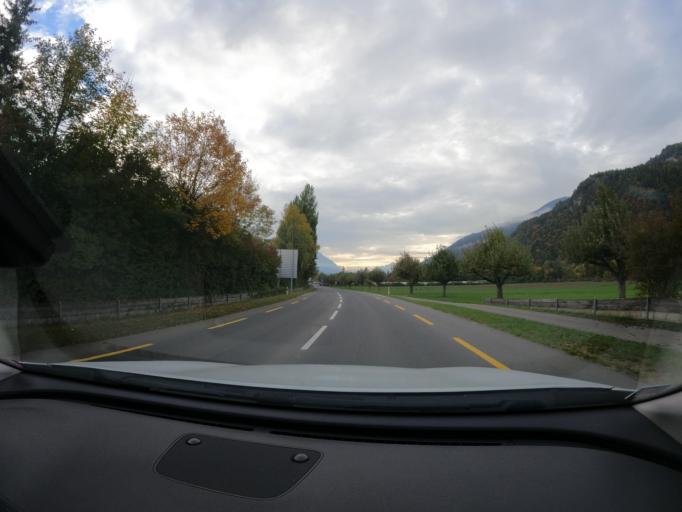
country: CH
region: Bern
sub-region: Interlaken-Oberhasli District
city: Darligen
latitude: 46.6802
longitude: 7.8228
